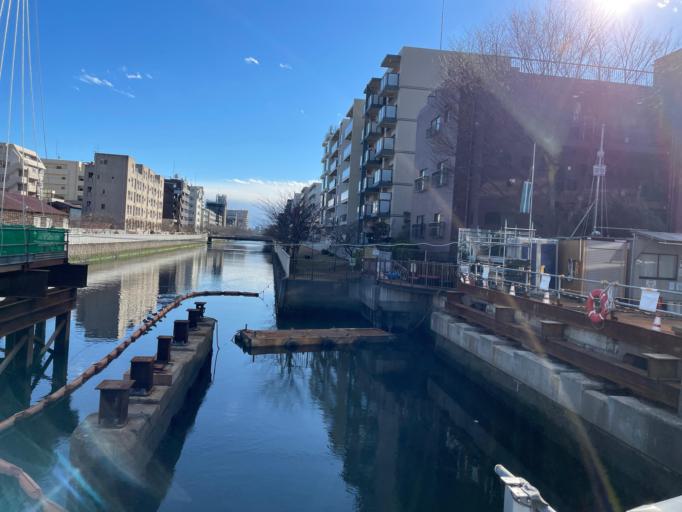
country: JP
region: Tokyo
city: Urayasu
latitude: 35.6921
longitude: 139.8090
